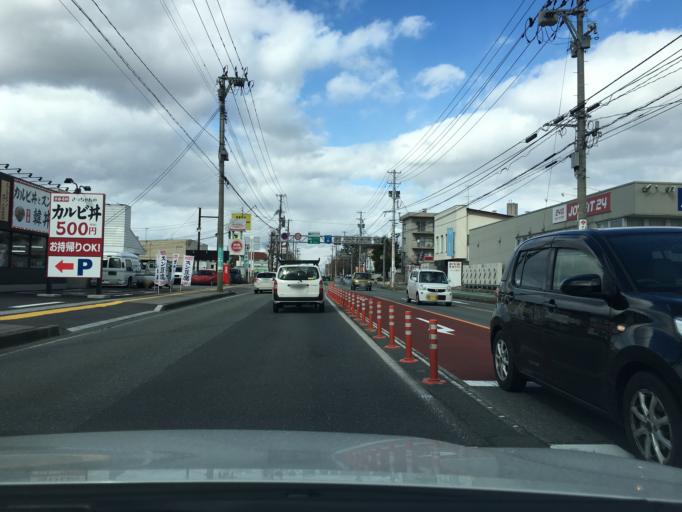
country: JP
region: Yamagata
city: Yamagata-shi
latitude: 38.2436
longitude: 140.3079
